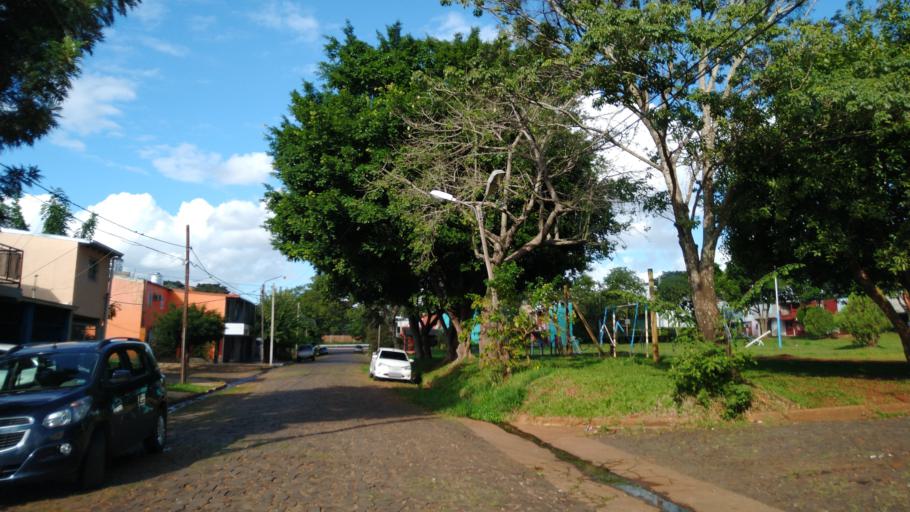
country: AR
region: Misiones
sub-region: Departamento de Capital
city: Posadas
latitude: -27.3585
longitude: -55.9247
